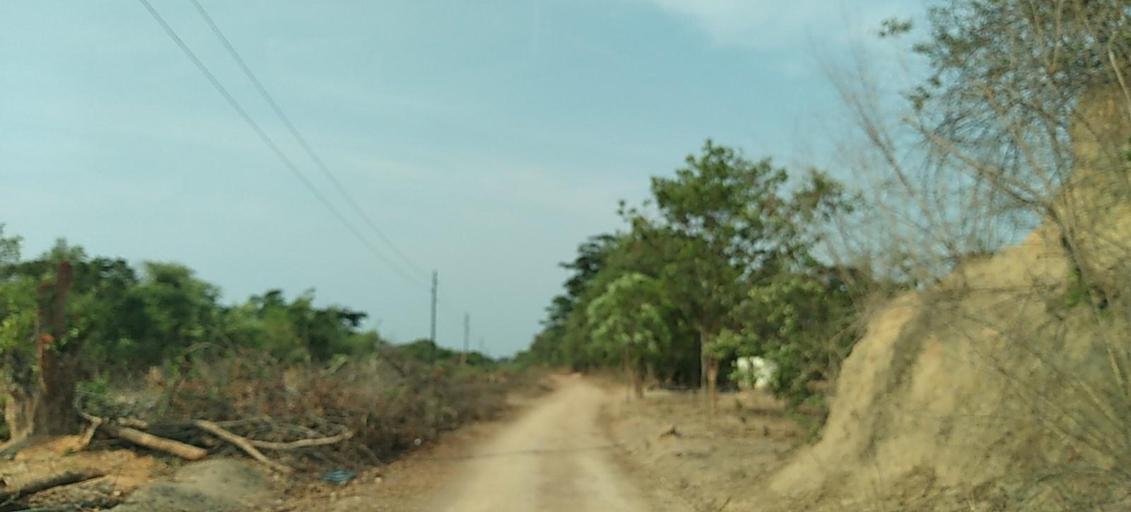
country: ZM
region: Copperbelt
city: Ndola
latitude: -13.2211
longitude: 28.6784
